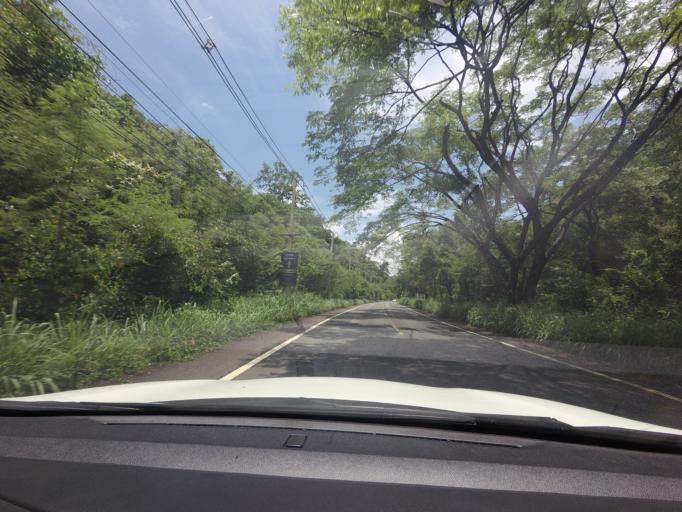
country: TH
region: Sara Buri
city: Muak Lek
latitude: 14.5742
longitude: 101.2786
